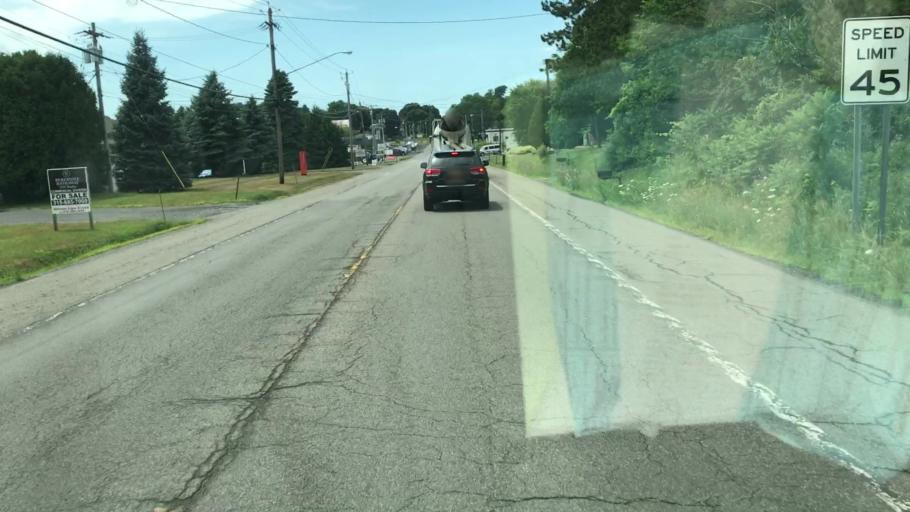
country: US
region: New York
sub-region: Onondaga County
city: Skaneateles
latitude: 42.9447
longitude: -76.4071
